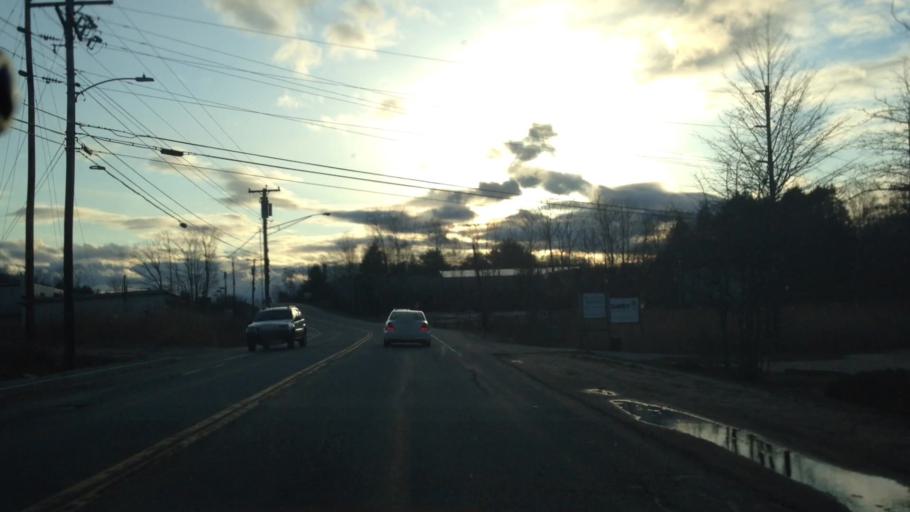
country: US
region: Maine
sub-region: Cumberland County
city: Westbrook
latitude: 43.6862
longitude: -70.3320
